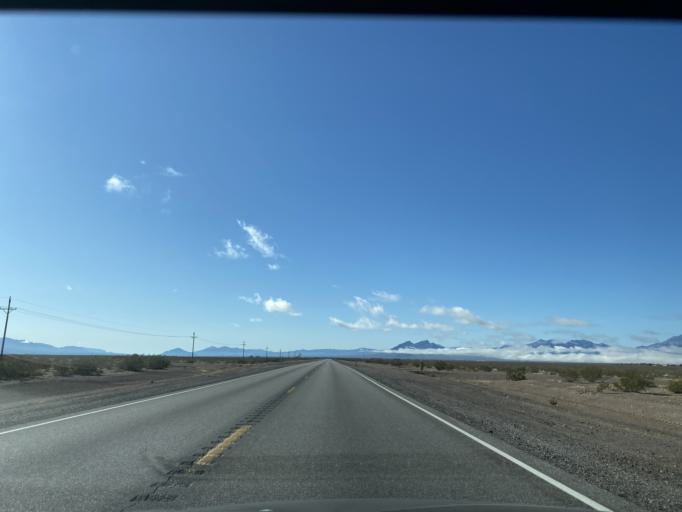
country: US
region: Nevada
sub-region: Nye County
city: Beatty
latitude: 36.5629
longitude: -116.4147
